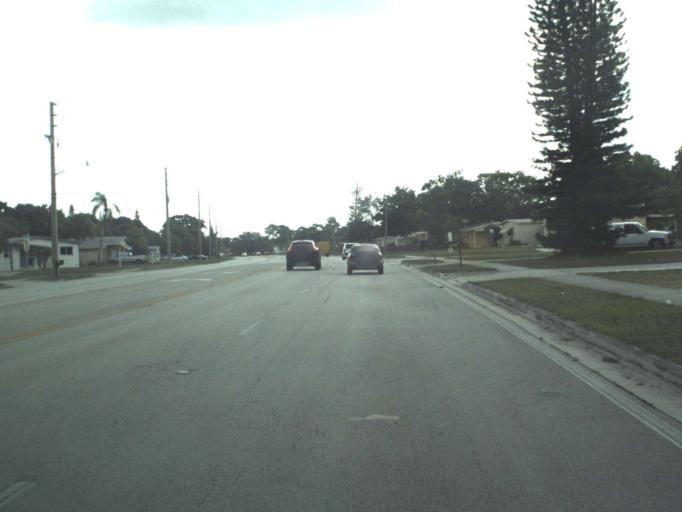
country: US
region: Florida
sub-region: Saint Lucie County
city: River Park
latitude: 27.3177
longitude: -80.3456
